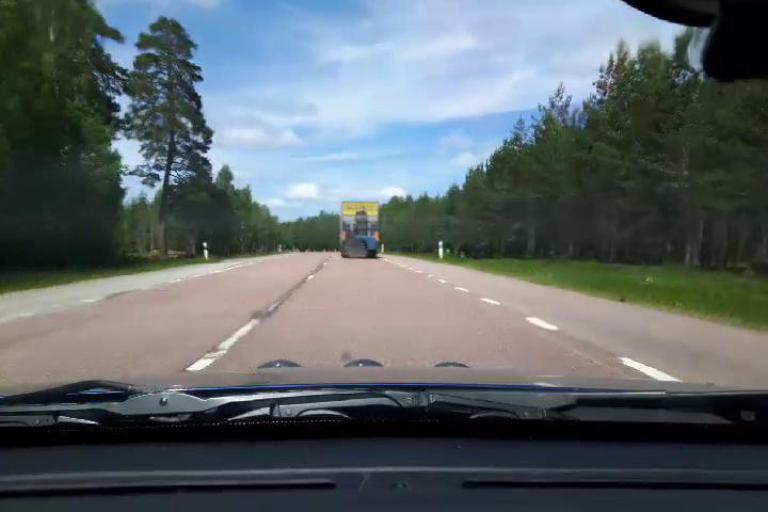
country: SE
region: Uppsala
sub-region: Osthammars Kommun
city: Bjorklinge
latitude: 60.1292
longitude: 17.5096
